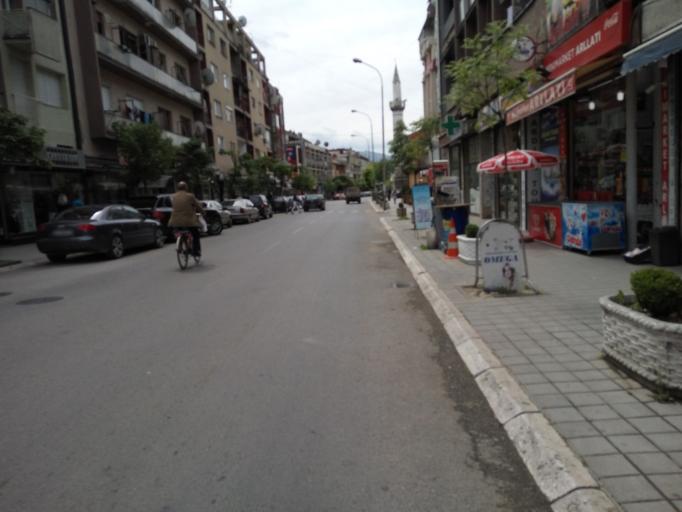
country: XK
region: Gjakova
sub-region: Komuna e Gjakoves
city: Gjakove
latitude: 42.3824
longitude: 20.4306
